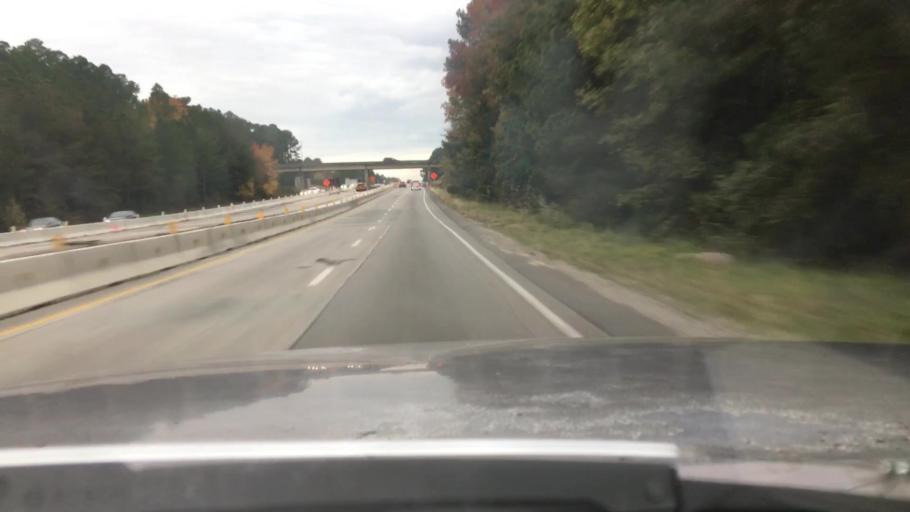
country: US
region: South Carolina
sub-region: Lexington County
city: Lexington
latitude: 33.9678
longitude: -81.2035
